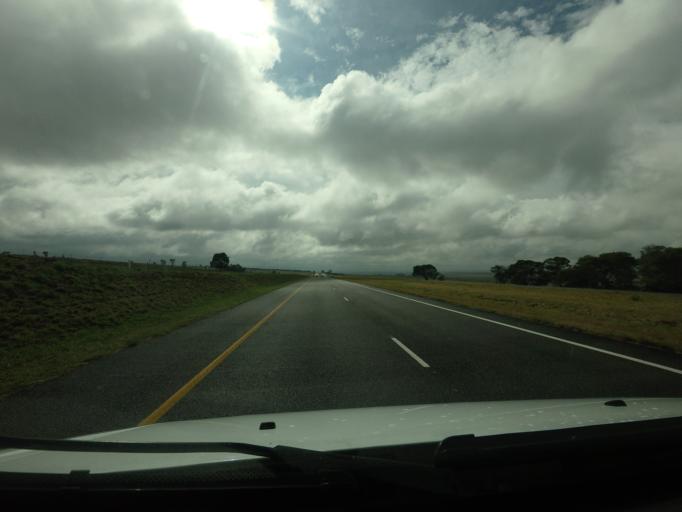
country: ZA
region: Gauteng
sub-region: City of Tshwane Metropolitan Municipality
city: Bronkhorstspruit
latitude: -25.7993
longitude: 28.6365
